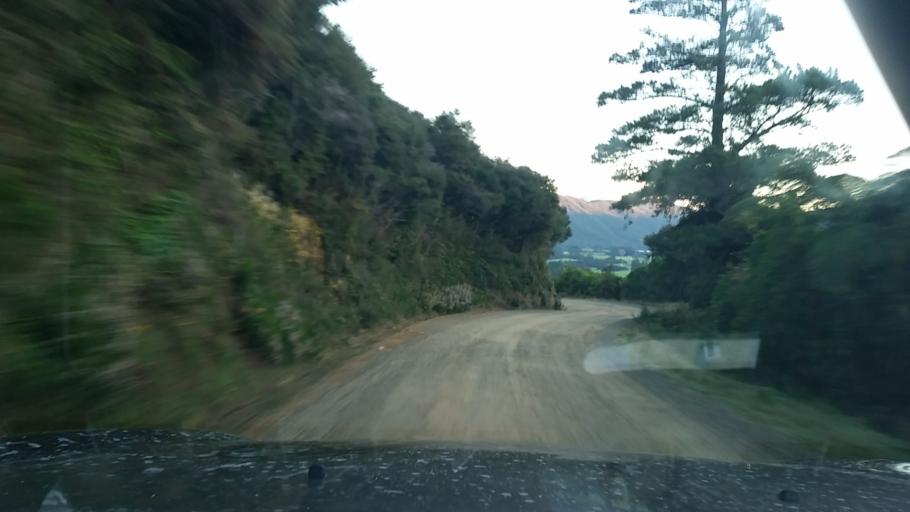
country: NZ
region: Marlborough
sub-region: Marlborough District
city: Picton
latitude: -41.1335
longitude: 174.1422
